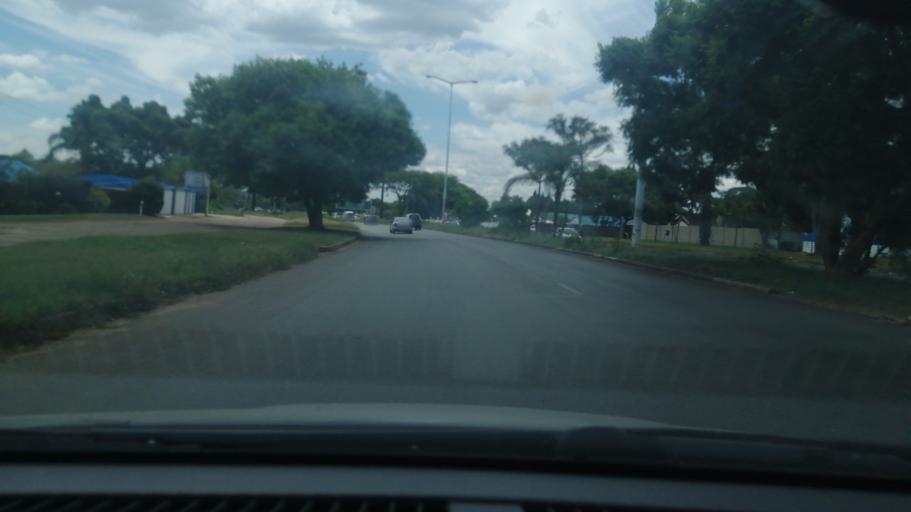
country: ZW
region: Harare
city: Harare
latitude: -17.8249
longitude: 31.0946
